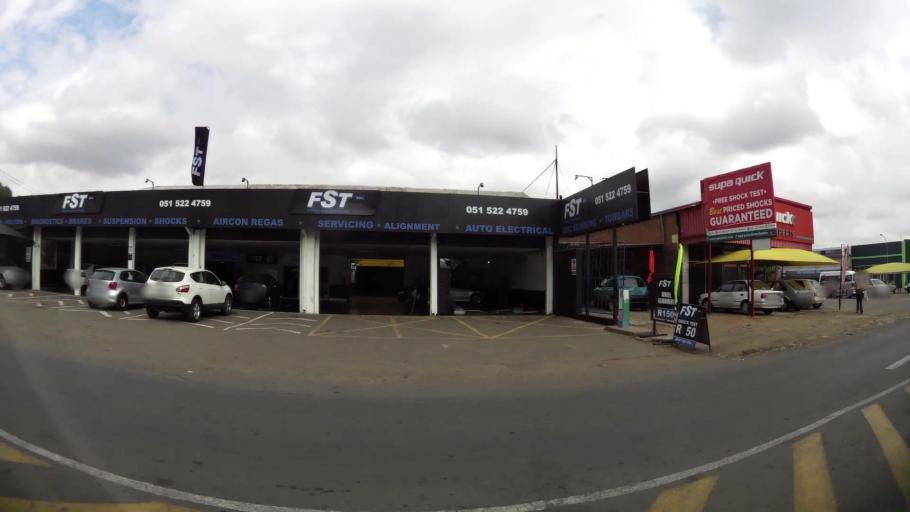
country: ZA
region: Orange Free State
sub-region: Mangaung Metropolitan Municipality
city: Bloemfontein
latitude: -29.1267
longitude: 26.2200
